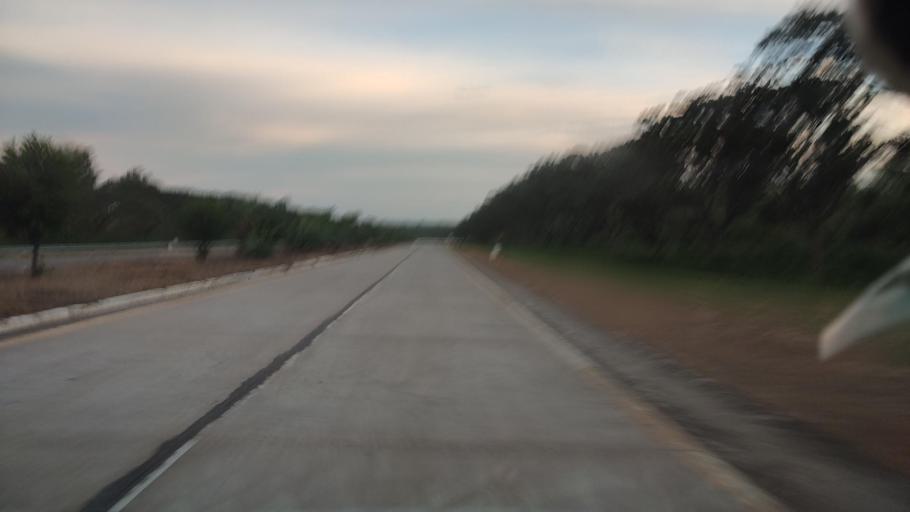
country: MM
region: Mandalay
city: Yamethin
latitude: 20.2797
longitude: 95.8916
